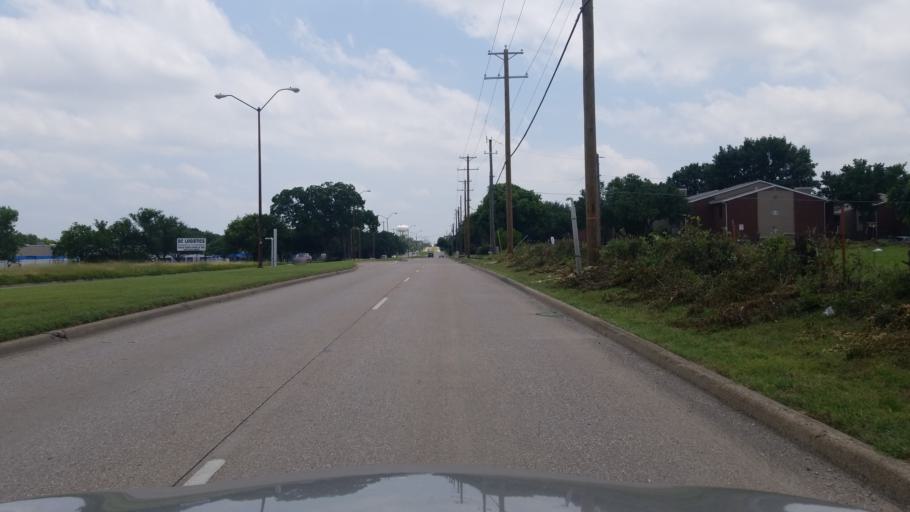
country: US
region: Texas
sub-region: Dallas County
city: Duncanville
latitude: 32.6879
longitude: -96.9087
